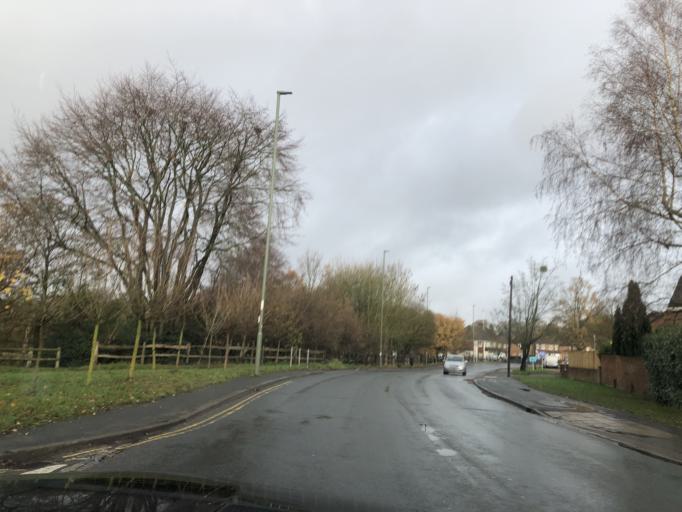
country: GB
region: England
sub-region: Hampshire
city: Farnborough
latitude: 51.2784
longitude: -0.7281
